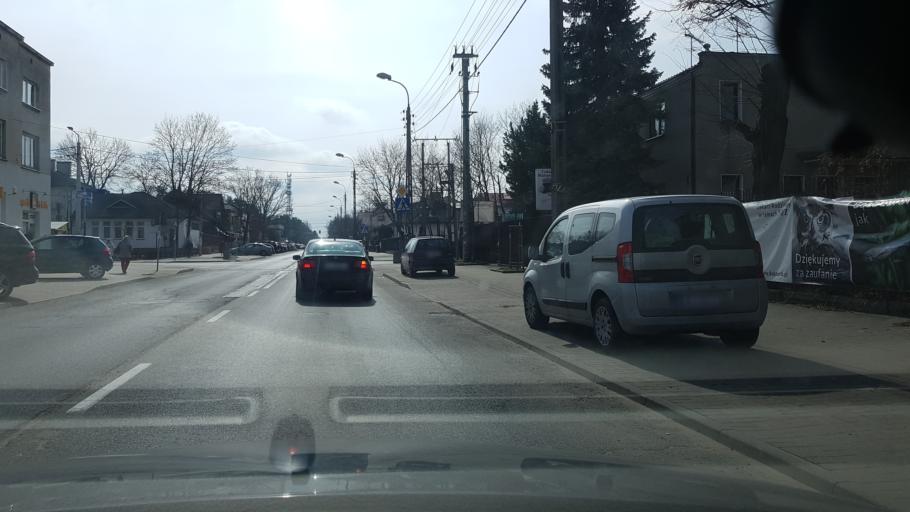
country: PL
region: Masovian Voivodeship
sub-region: Warszawa
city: Wesola
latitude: 52.2531
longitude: 21.2240
